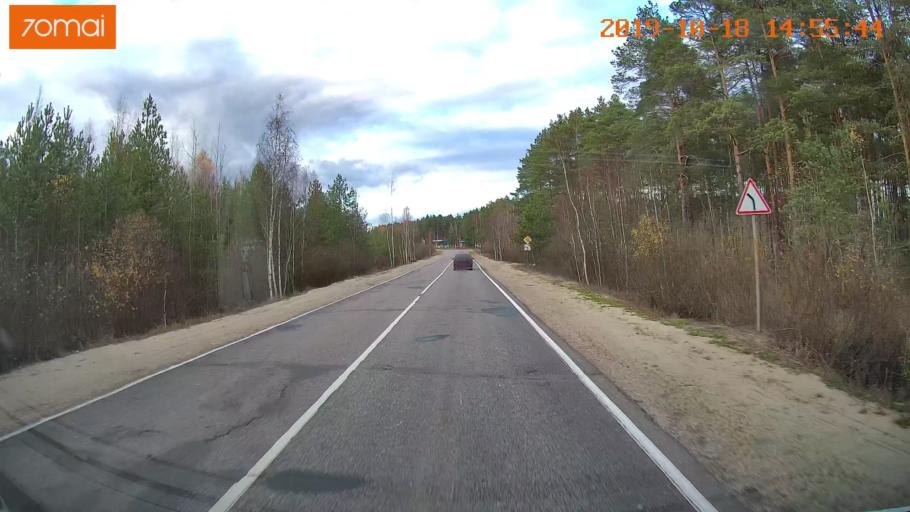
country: RU
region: Vladimir
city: Kurlovo
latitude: 55.4564
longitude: 40.5898
